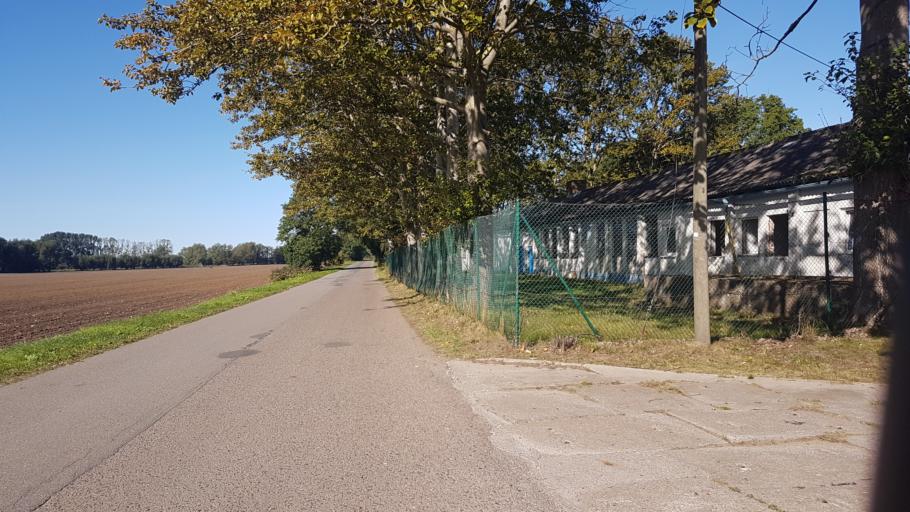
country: DE
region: Mecklenburg-Vorpommern
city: Sagard
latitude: 54.5197
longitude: 13.5293
